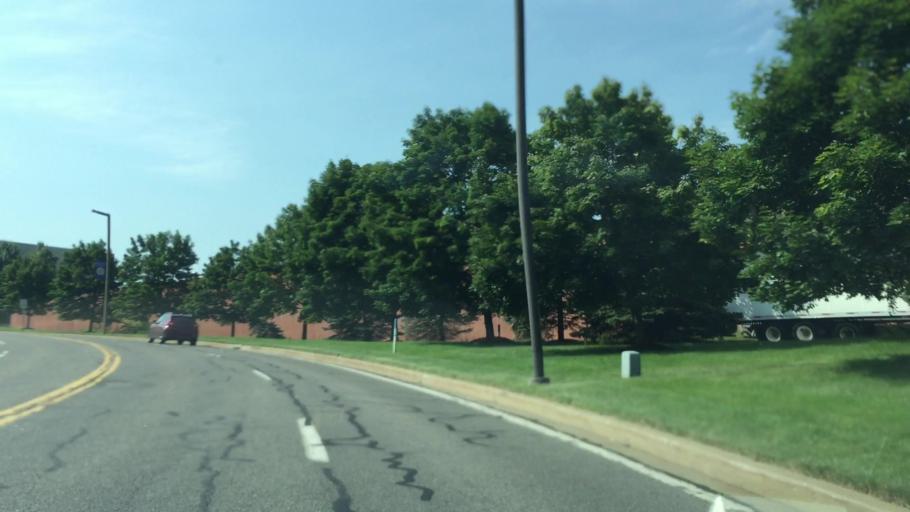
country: US
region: Pennsylvania
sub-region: Allegheny County
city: Enlow
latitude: 40.4526
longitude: -80.1936
